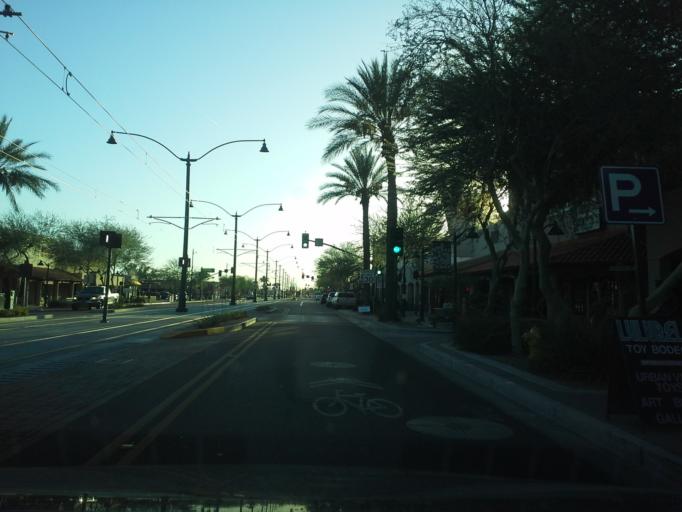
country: US
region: Arizona
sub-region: Maricopa County
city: Mesa
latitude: 33.4153
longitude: -111.8351
